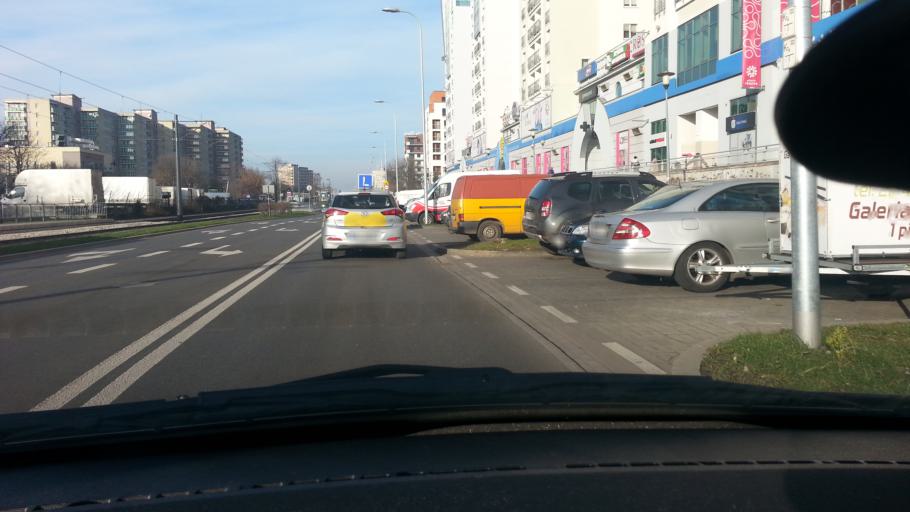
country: PL
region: Masovian Voivodeship
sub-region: Warszawa
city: Targowek
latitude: 52.2887
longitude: 21.0306
